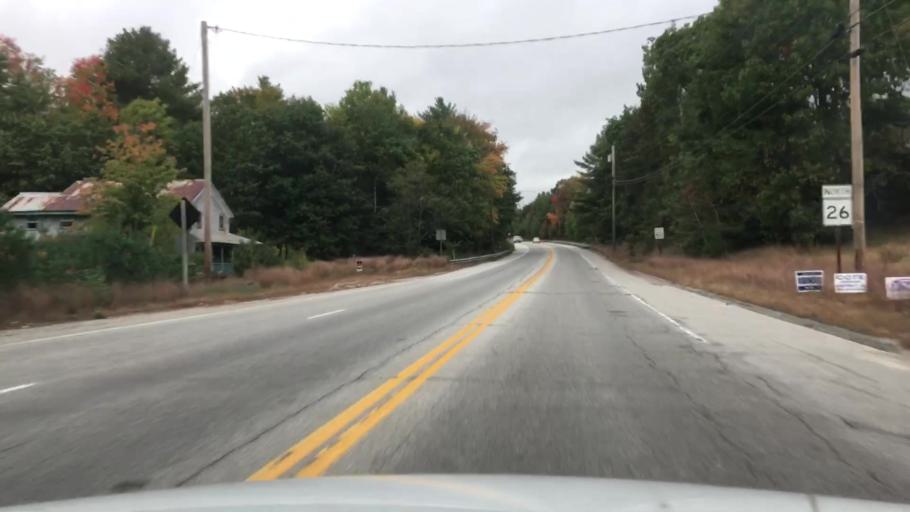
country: US
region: Maine
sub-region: Oxford County
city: Oxford
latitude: 44.1640
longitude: -70.4994
